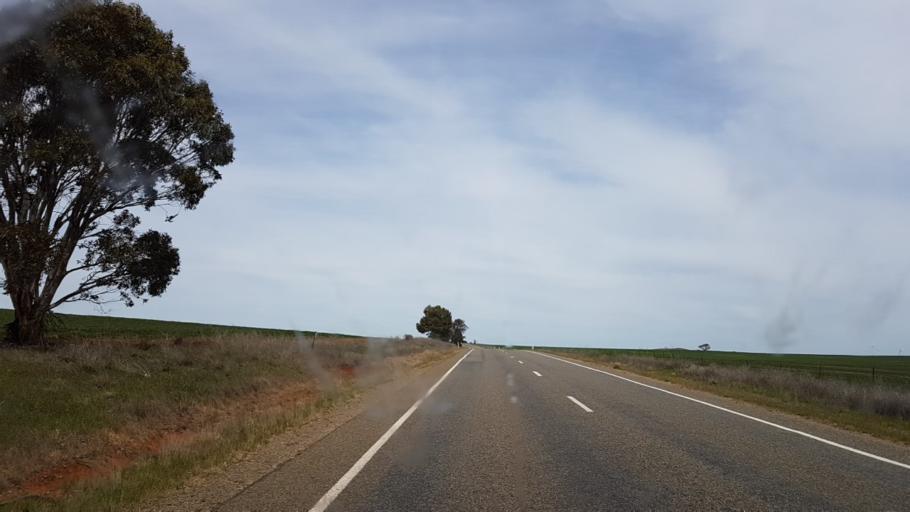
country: AU
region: South Australia
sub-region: Northern Areas
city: Jamestown
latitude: -33.0997
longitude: 138.6194
